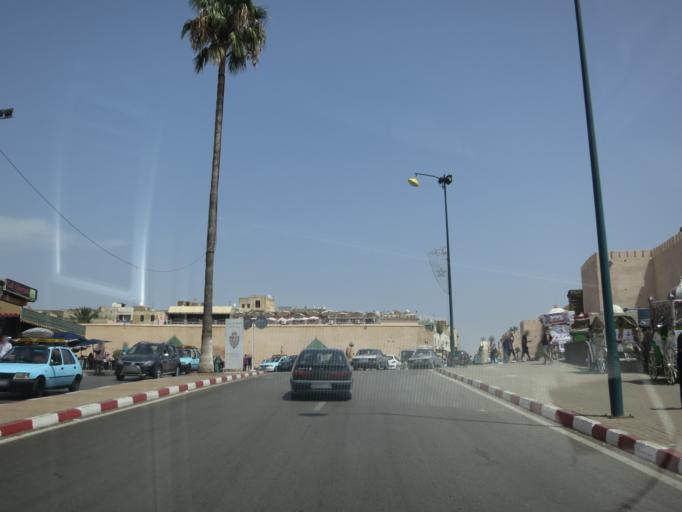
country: MA
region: Meknes-Tafilalet
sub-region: Meknes
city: Meknes
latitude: 33.8922
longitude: -5.5658
